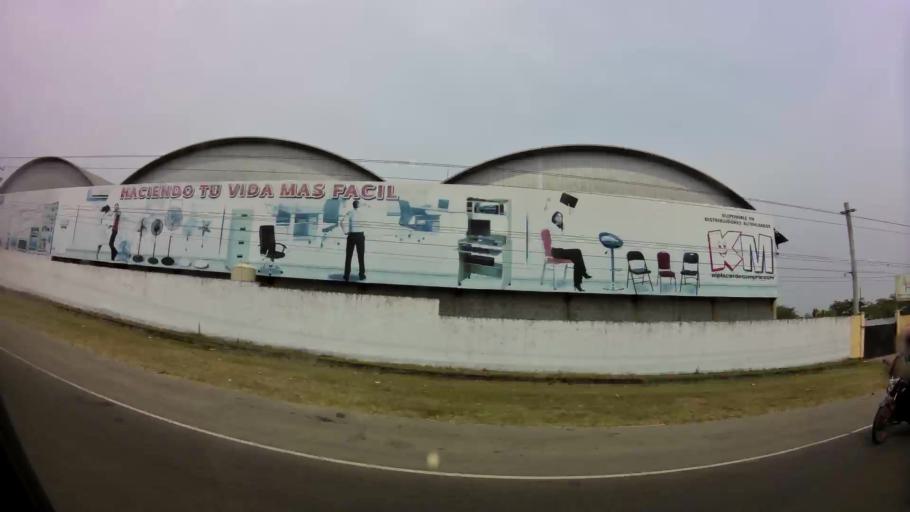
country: HN
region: Cortes
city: Nuevo Chamelecon
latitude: 15.3639
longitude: -87.9854
